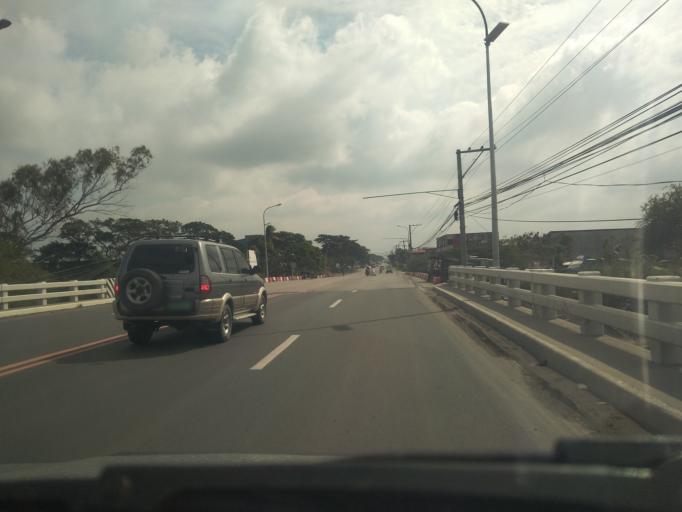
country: PH
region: Central Luzon
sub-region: Province of Pampanga
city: Pau
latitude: 15.0047
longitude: 120.7188
